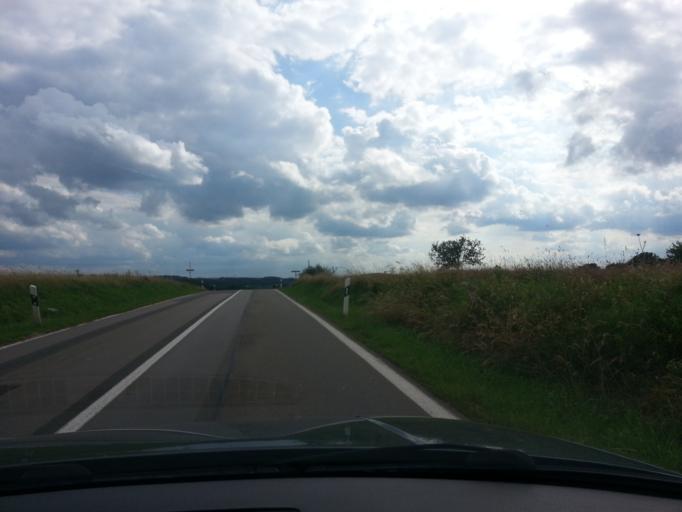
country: DE
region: Saarland
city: Mainzweiler
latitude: 49.4094
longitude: 7.1122
